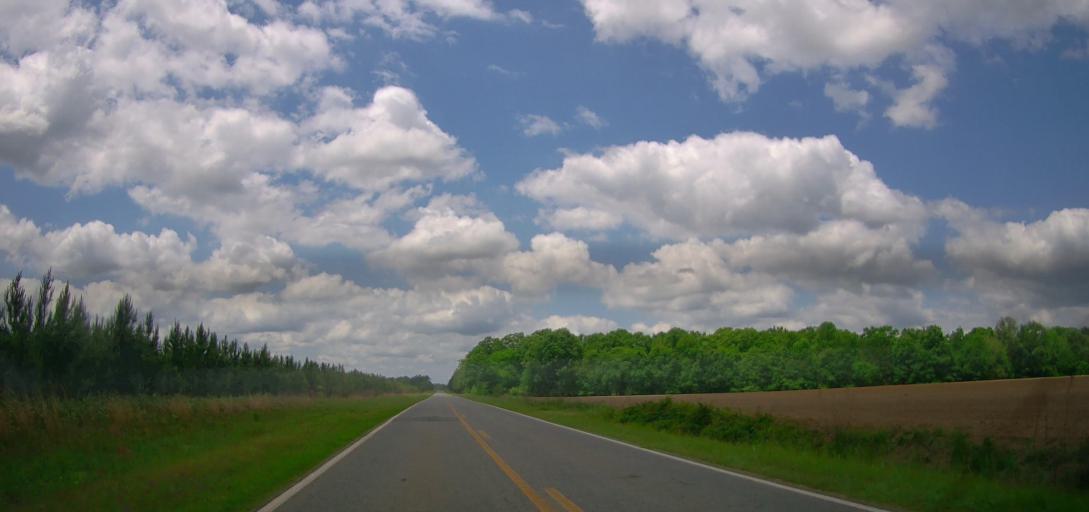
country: US
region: Georgia
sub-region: Laurens County
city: Dublin
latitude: 32.6032
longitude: -82.9789
